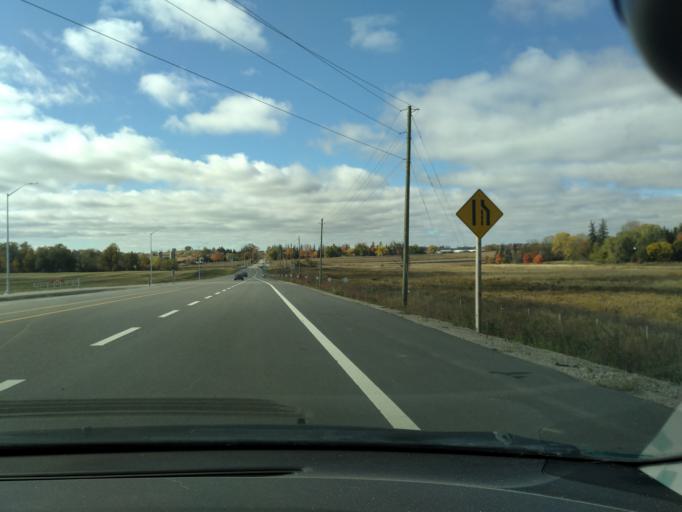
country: CA
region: Ontario
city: Bradford West Gwillimbury
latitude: 44.0744
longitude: -79.6280
